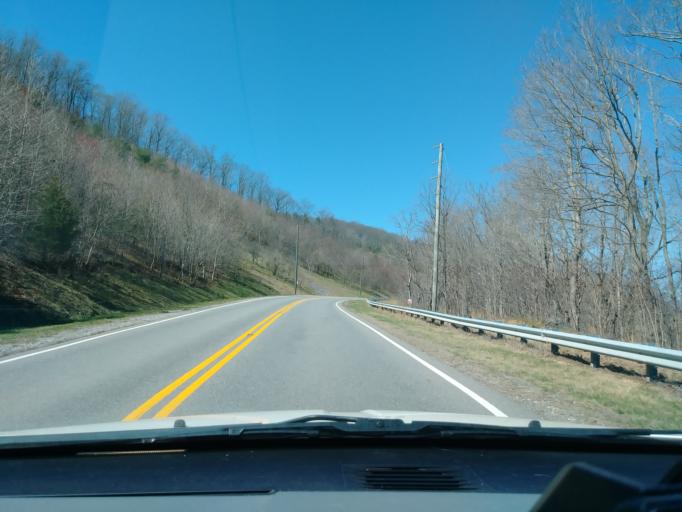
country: US
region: North Carolina
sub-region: Madison County
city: Marshall
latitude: 35.8955
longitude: -82.8383
